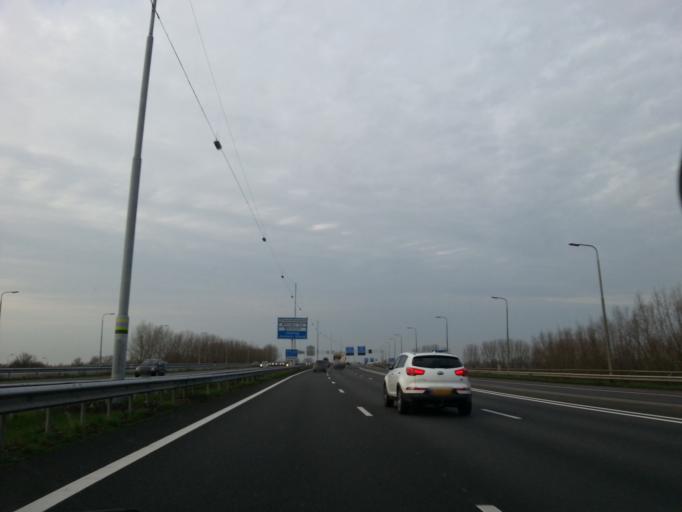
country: NL
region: Gelderland
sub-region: Gemeente Westervoort
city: Westervoort
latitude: 51.9693
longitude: 5.9968
